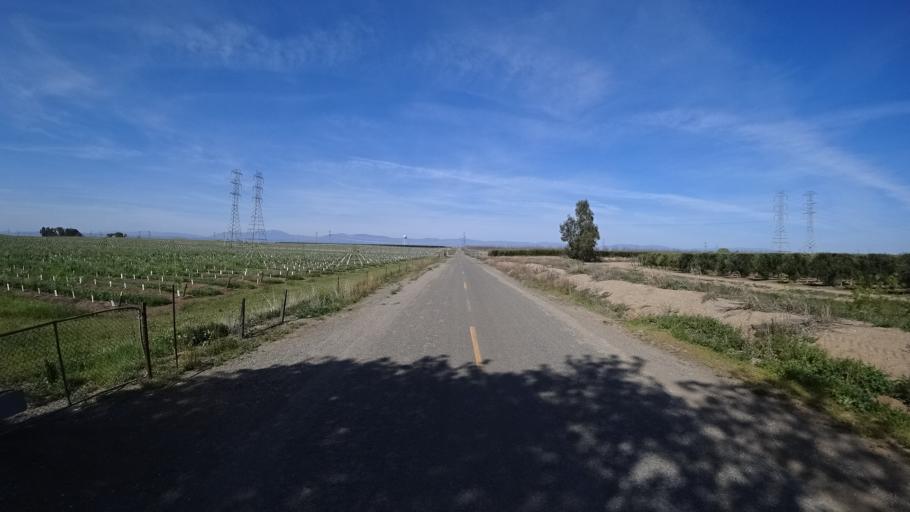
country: US
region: California
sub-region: Glenn County
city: Willows
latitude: 39.6116
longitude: -122.2626
